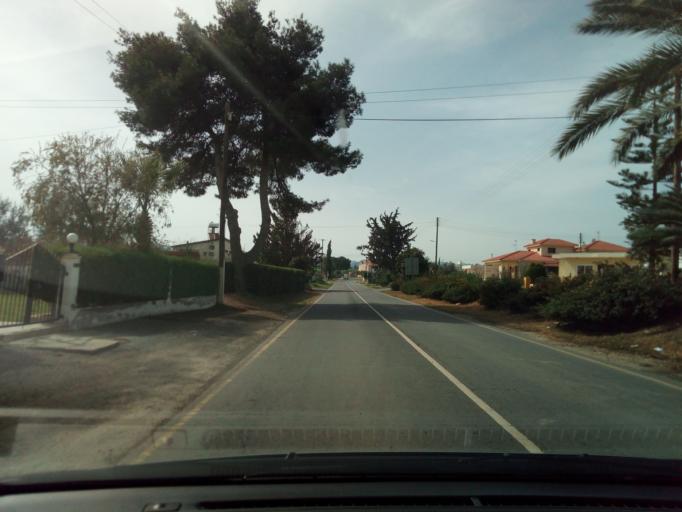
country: CY
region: Lefkosia
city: Psimolofou
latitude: 35.0737
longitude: 33.2472
